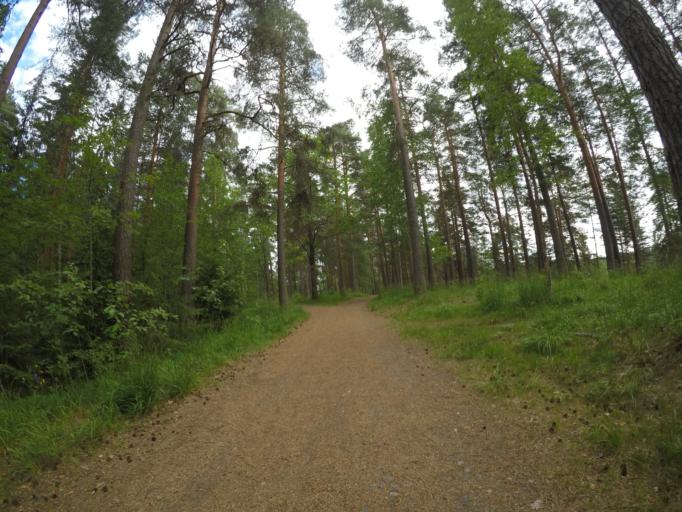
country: FI
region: Haeme
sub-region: Haemeenlinna
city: Haemeenlinna
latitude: 60.9966
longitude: 24.4204
